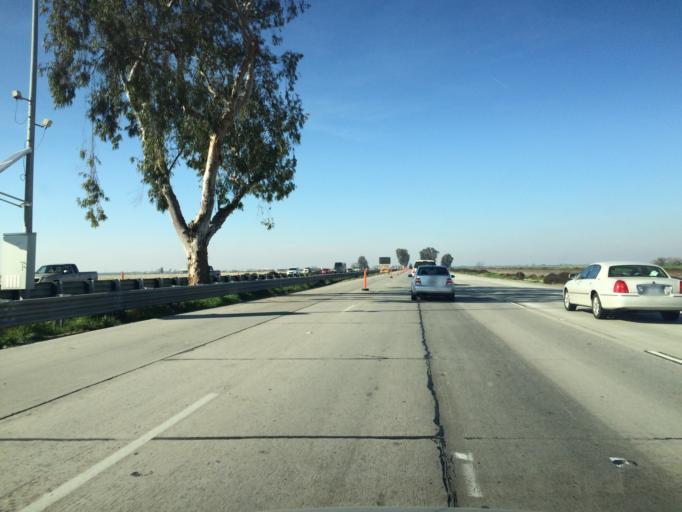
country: US
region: California
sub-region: Tulare County
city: Goshen
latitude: 36.4085
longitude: -119.4590
